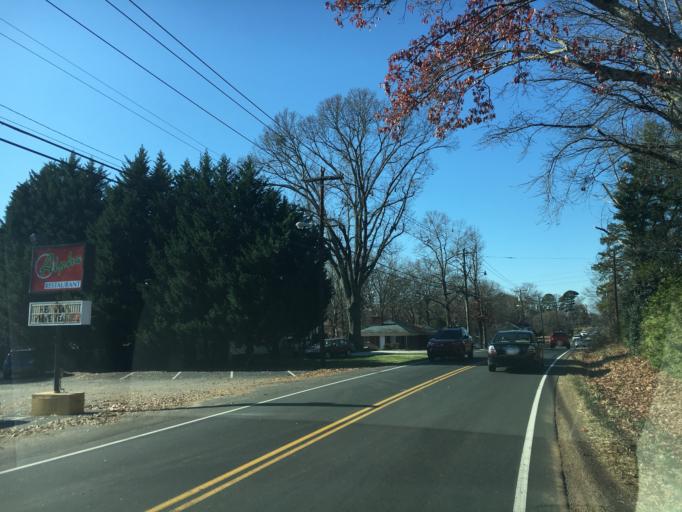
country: US
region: South Carolina
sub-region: Greenville County
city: Wade Hampton
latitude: 34.9033
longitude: -82.3257
